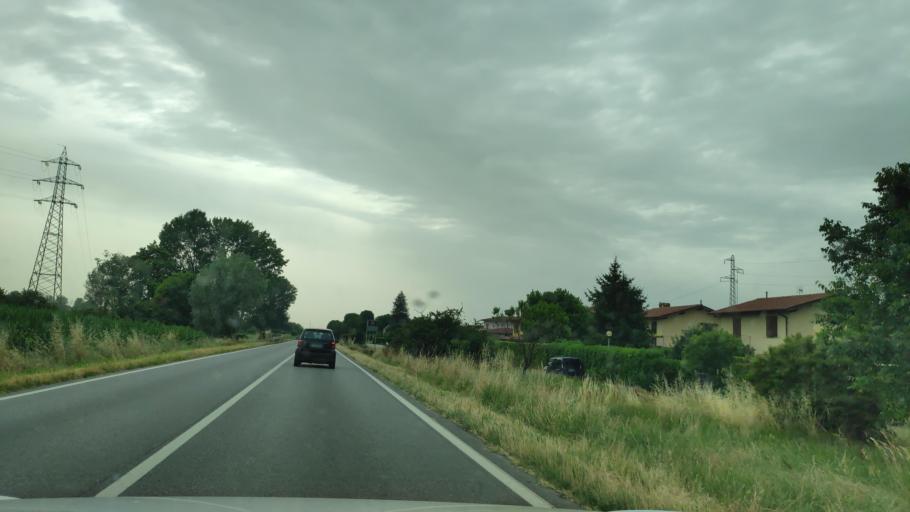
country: IT
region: Lombardy
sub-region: Provincia di Cremona
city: Romanengo
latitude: 45.3747
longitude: 9.7817
